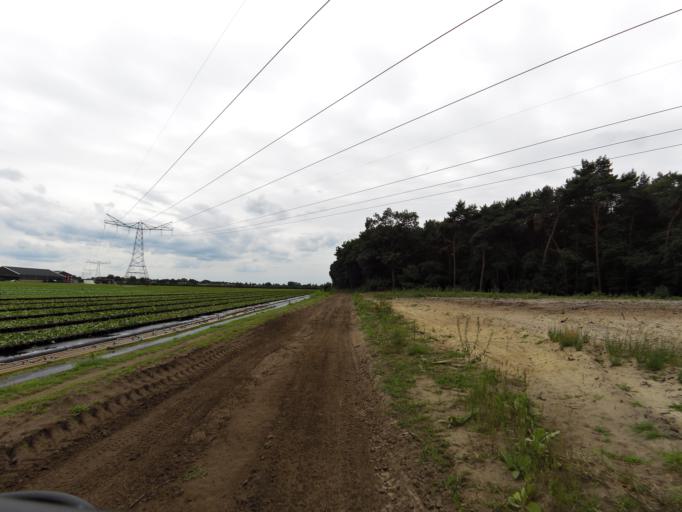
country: NL
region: North Brabant
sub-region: Gemeente Son en Breugel
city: Breugel
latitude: 51.5415
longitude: 5.5372
